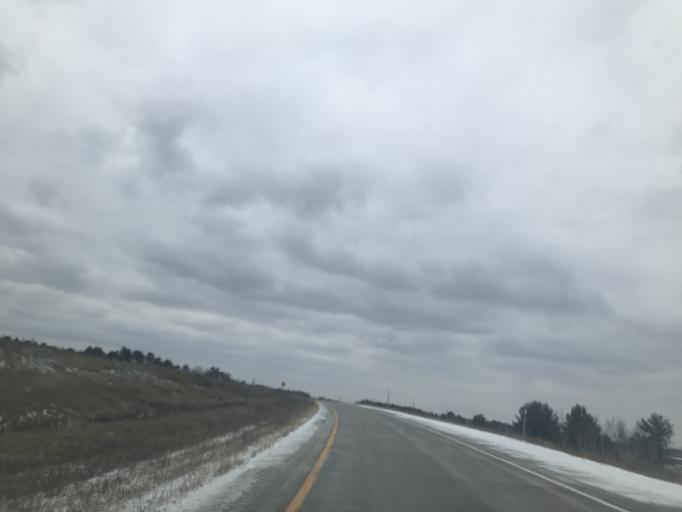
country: US
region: Wisconsin
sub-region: Marinette County
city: Peshtigo
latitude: 45.0584
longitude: -87.7168
